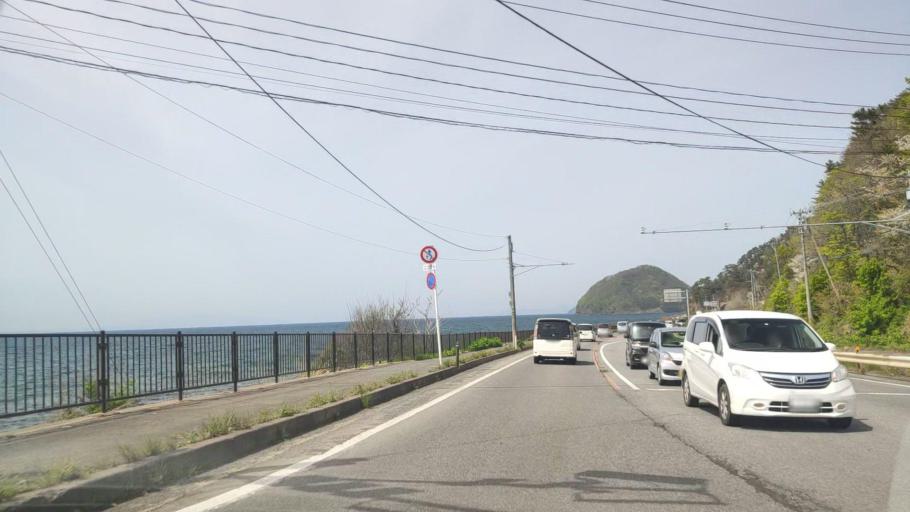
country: JP
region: Aomori
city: Aomori Shi
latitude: 40.8777
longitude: 140.8499
